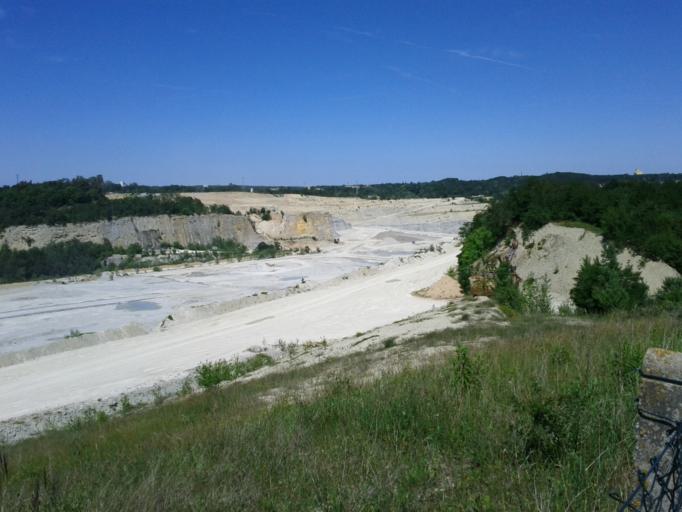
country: DE
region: Brandenburg
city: Woltersdorf
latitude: 52.4760
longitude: 13.7938
